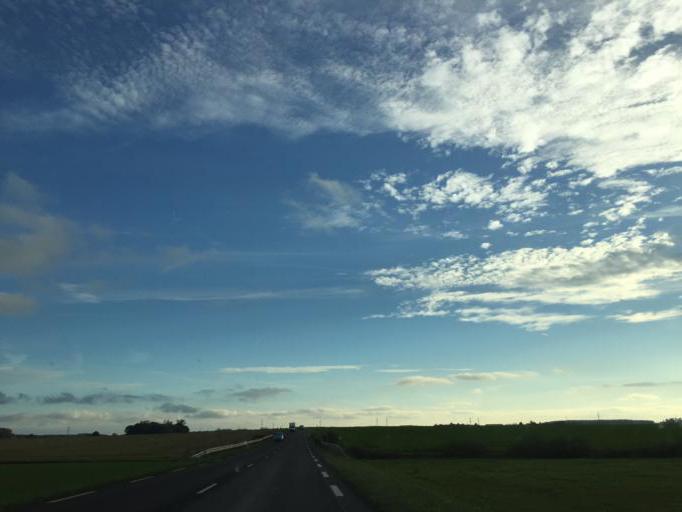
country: FR
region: Ile-de-France
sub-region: Departement de Seine-et-Marne
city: Jouy-le-Chatel
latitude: 48.6306
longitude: 3.1024
